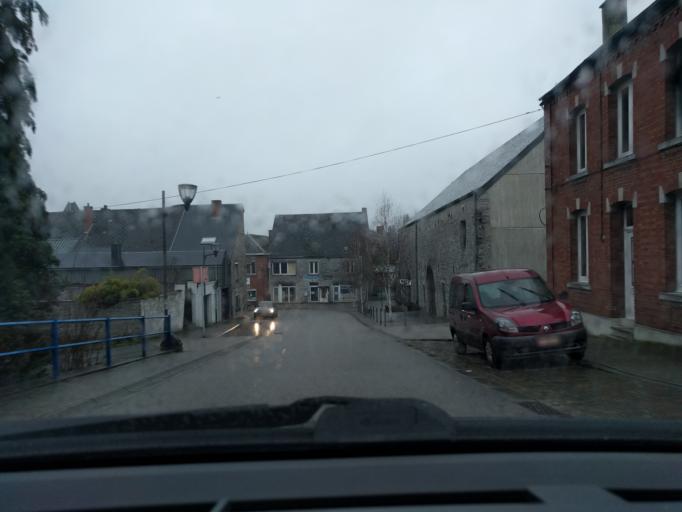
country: BE
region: Wallonia
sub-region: Province de Namur
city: Couvin
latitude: 50.0521
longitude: 4.4977
